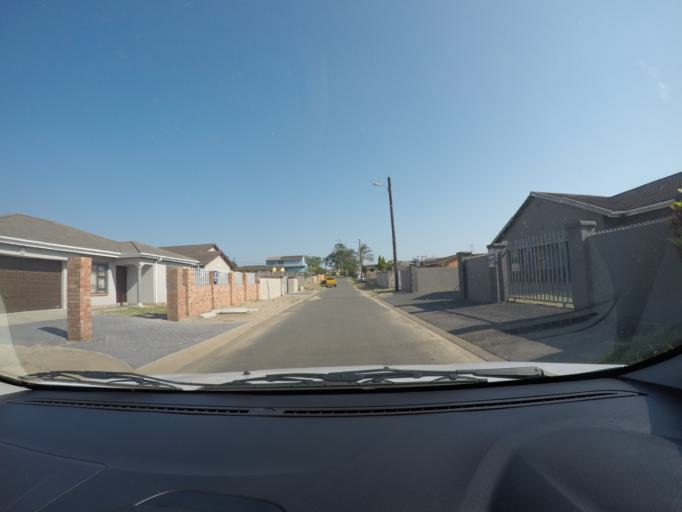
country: ZA
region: KwaZulu-Natal
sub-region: uThungulu District Municipality
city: Richards Bay
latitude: -28.7230
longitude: 32.0362
